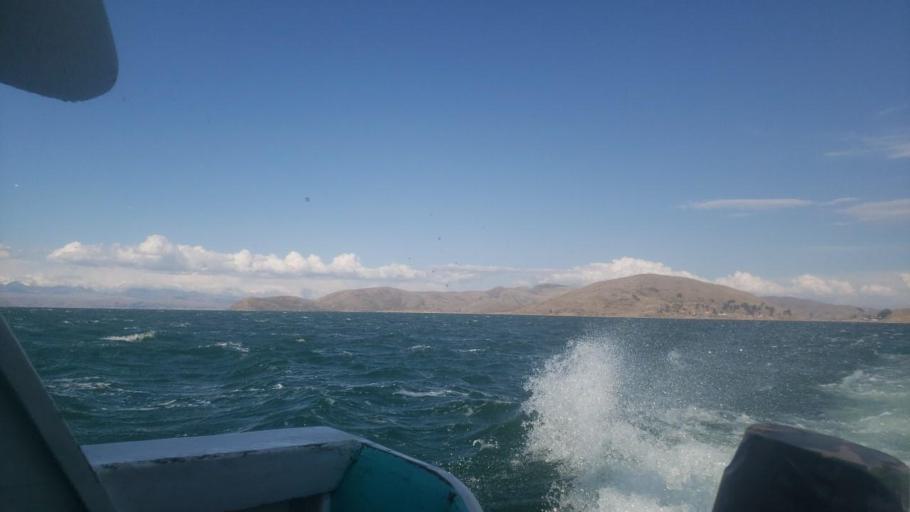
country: BO
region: La Paz
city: Huatajata
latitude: -16.3165
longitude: -68.7413
